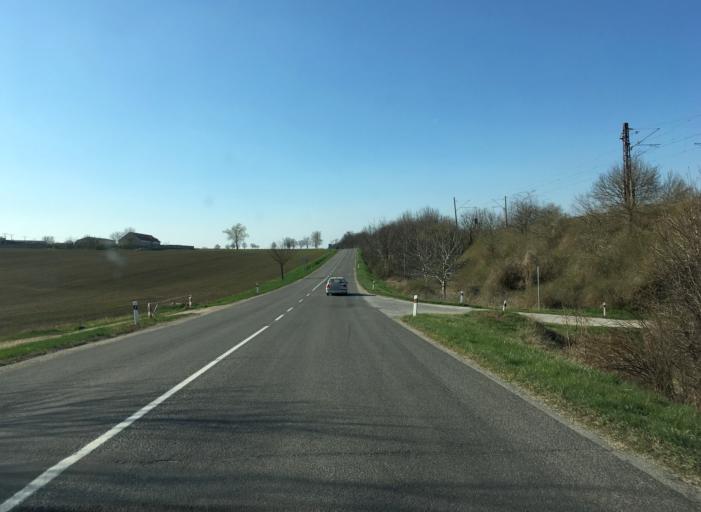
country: SK
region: Nitriansky
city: Svodin
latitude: 47.8733
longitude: 18.4520
